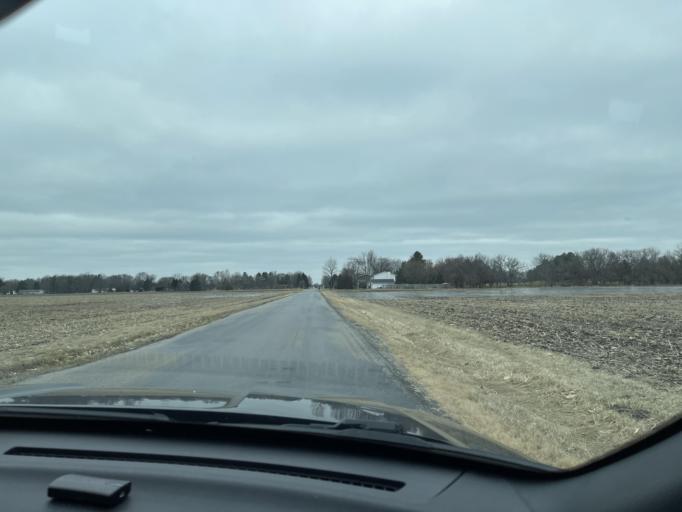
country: US
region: Illinois
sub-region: Sangamon County
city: Jerome
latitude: 39.7799
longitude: -89.7535
